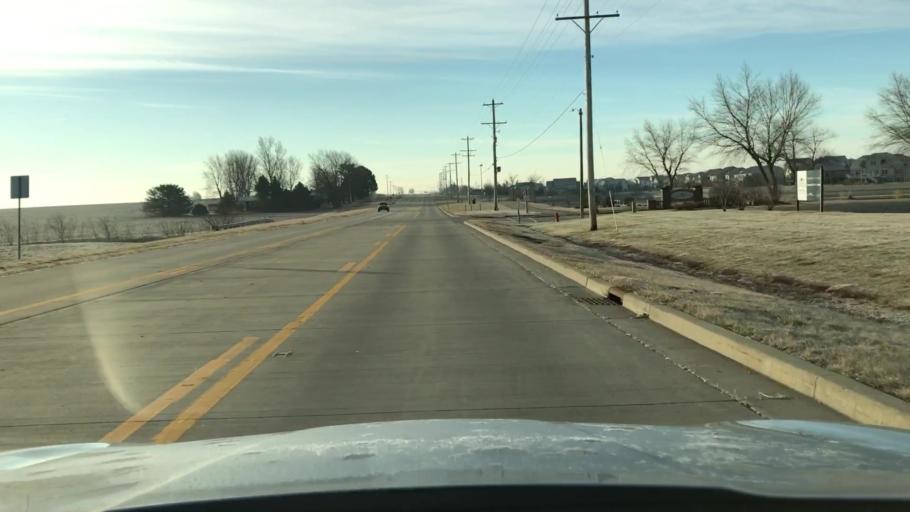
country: US
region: Illinois
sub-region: McLean County
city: Normal
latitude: 40.5578
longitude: -88.9446
